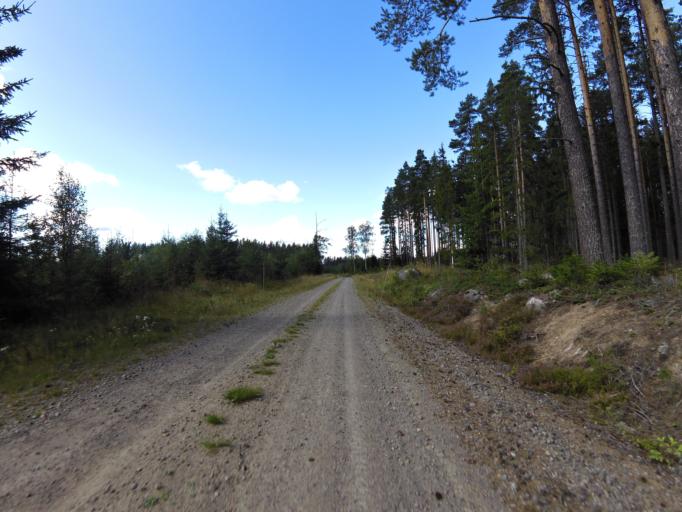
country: SE
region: Gaevleborg
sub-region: Ockelbo Kommun
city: Ockelbo
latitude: 60.8110
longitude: 16.7711
